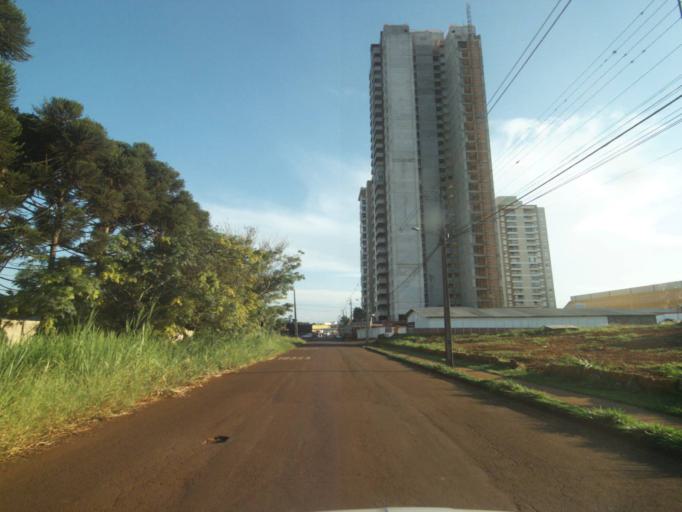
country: BR
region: Parana
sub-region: Londrina
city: Londrina
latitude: -23.3363
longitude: -51.1859
